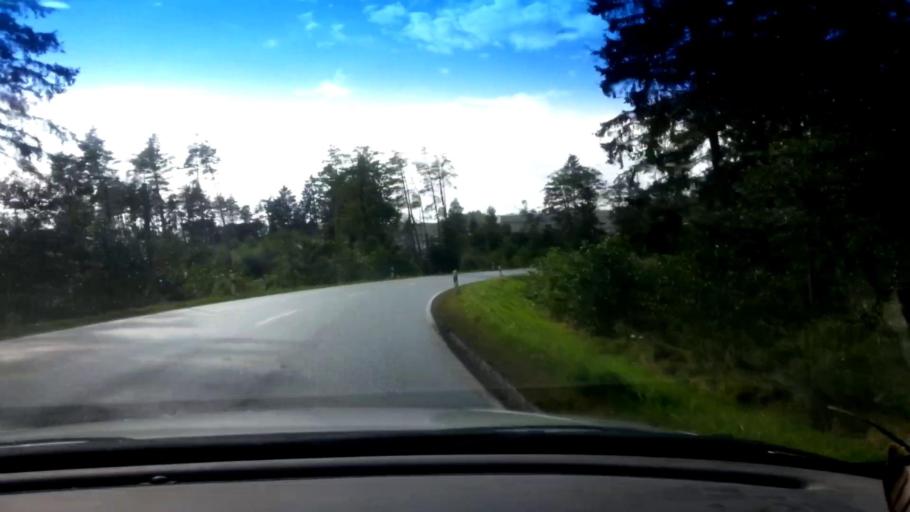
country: DE
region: Bavaria
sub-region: Upper Palatinate
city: Pechbrunn
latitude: 49.9933
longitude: 12.2101
